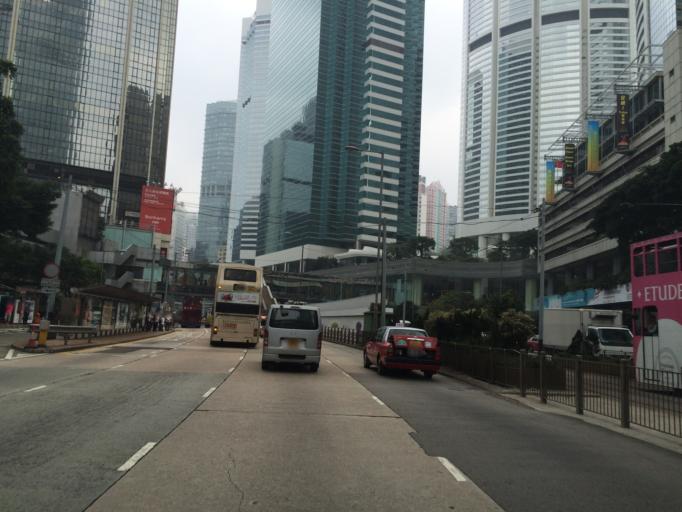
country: HK
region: Central and Western
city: Central
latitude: 22.2788
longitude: 114.1636
